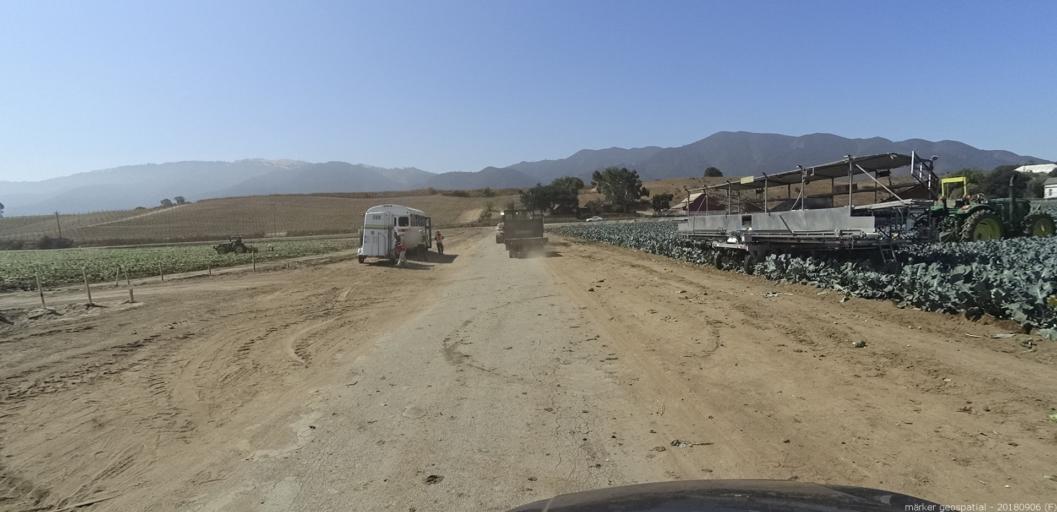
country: US
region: California
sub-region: Monterey County
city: Salinas
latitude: 36.5969
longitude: -121.6185
